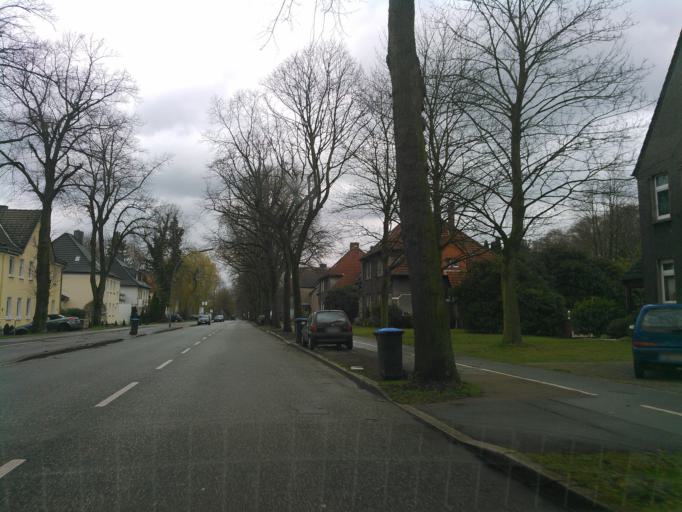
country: DE
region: North Rhine-Westphalia
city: Marl
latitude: 51.6038
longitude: 7.0725
